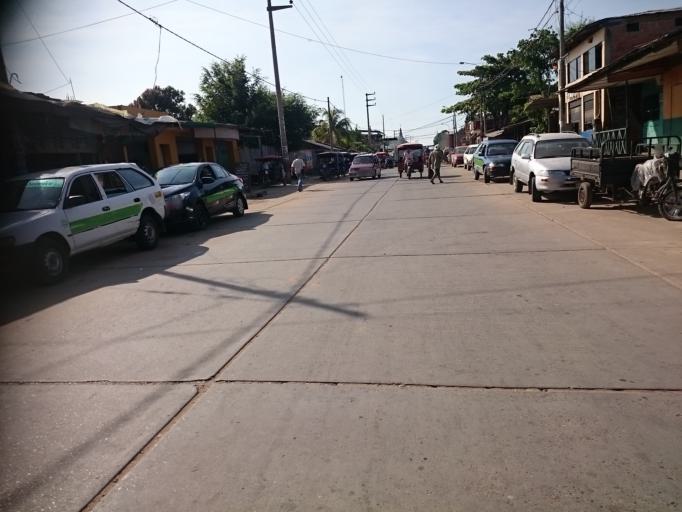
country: PE
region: Ucayali
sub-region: Provincia de Coronel Portillo
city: Puerto Callao
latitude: -8.3528
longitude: -74.5774
